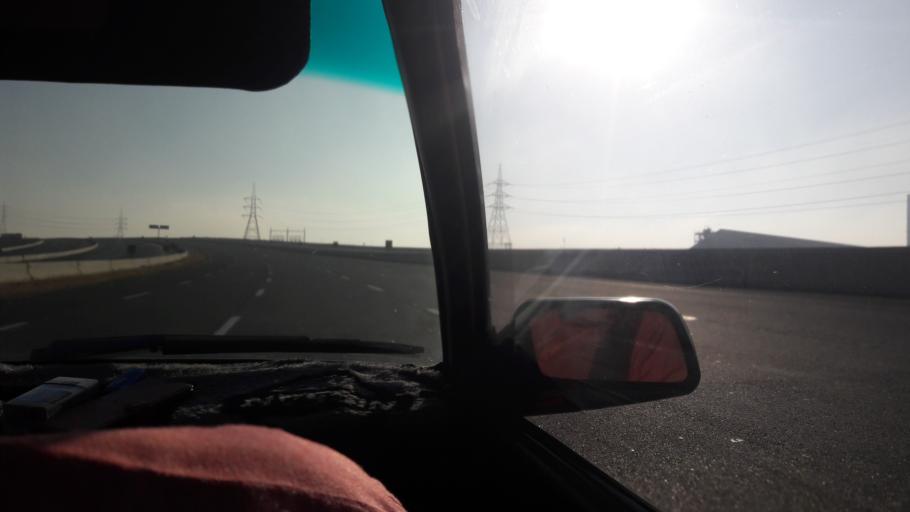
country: EG
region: Muhafazat al Qahirah
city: Halwan
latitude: 29.9207
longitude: 31.5205
